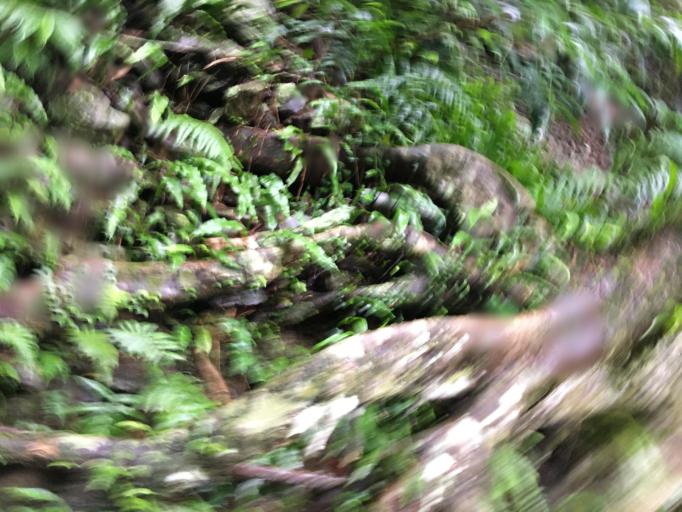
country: TW
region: Taiwan
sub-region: Yilan
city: Yilan
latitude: 24.8391
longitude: 121.7724
